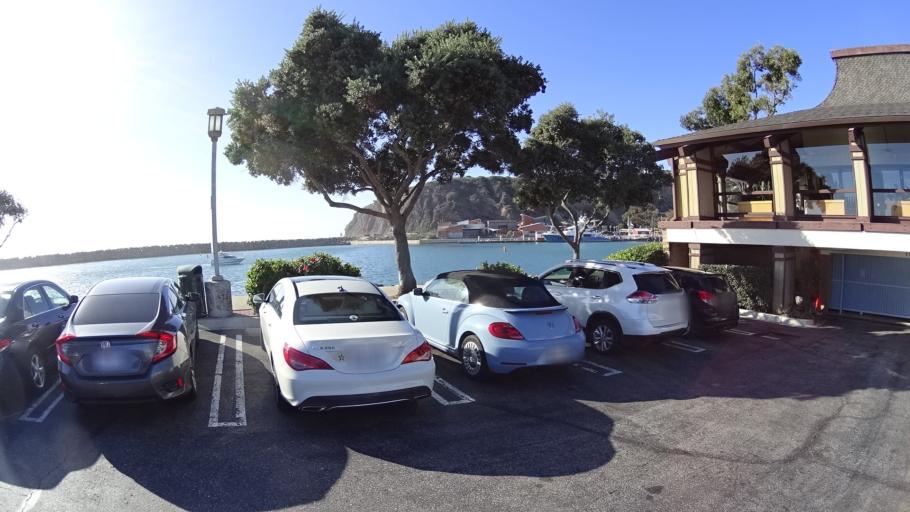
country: US
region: California
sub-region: Orange County
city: Dana Point
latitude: 33.4603
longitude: -117.7043
